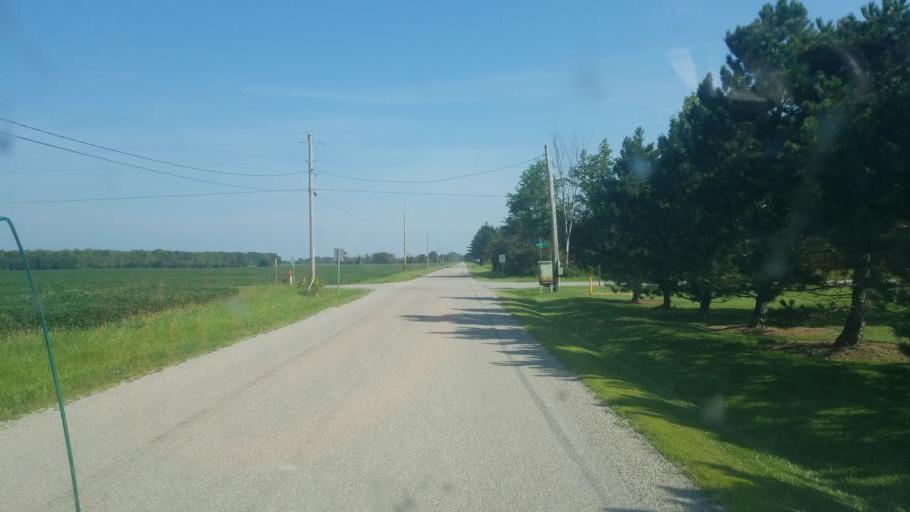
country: US
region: Ohio
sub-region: Lorain County
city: Wellington
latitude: 41.1153
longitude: -82.1804
